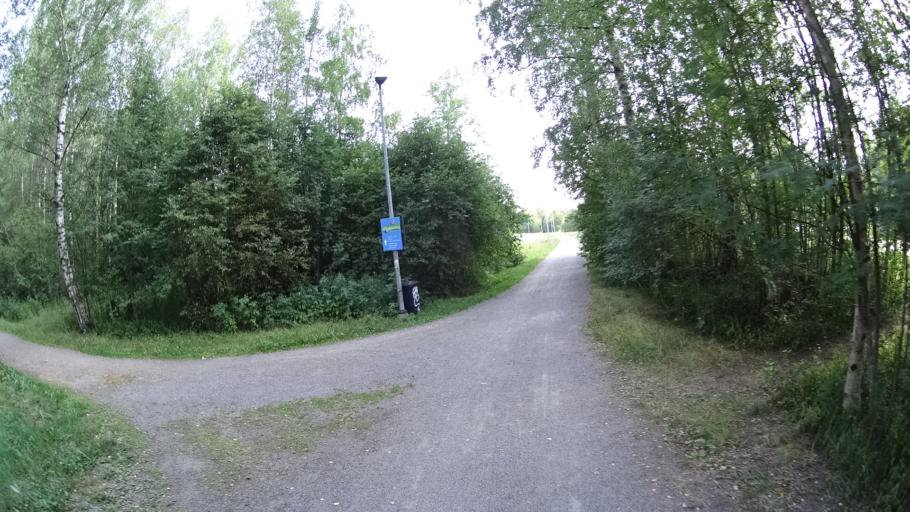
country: FI
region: Uusimaa
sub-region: Porvoo
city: Porvoo
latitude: 60.4020
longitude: 25.6449
